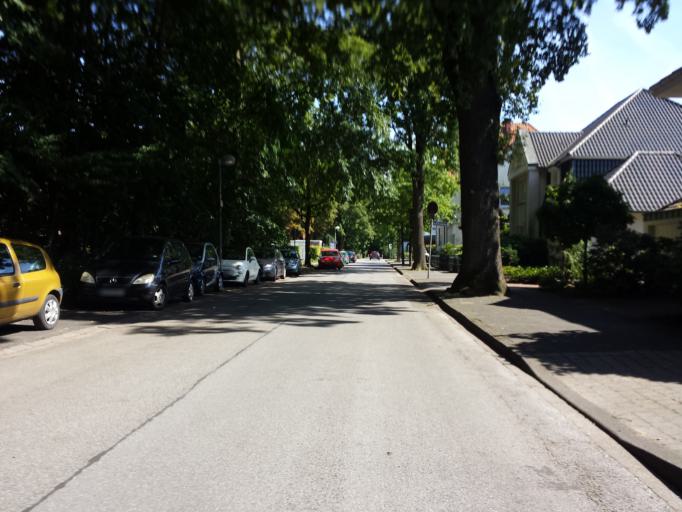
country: DE
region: North Rhine-Westphalia
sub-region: Regierungsbezirk Detmold
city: Guetersloh
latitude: 51.8962
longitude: 8.3848
